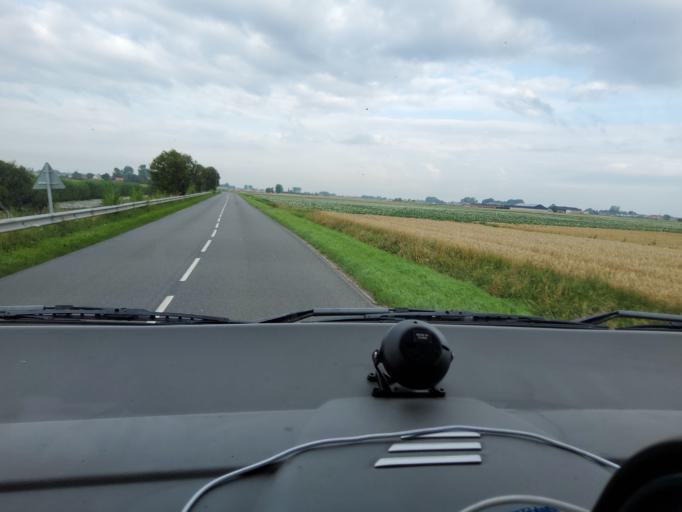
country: FR
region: Nord-Pas-de-Calais
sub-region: Departement du Nord
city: Steene
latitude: 50.9701
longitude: 2.3724
